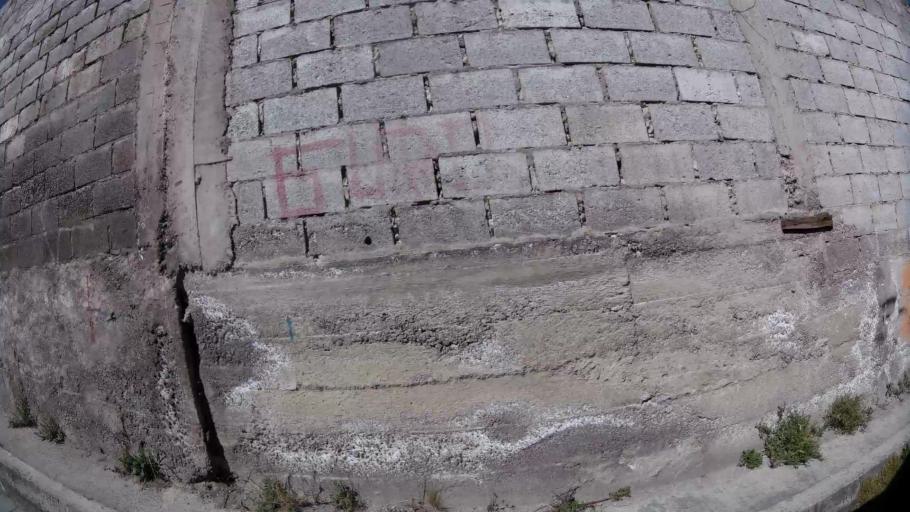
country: EC
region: Pichincha
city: Quito
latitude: -0.1204
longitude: -78.4797
